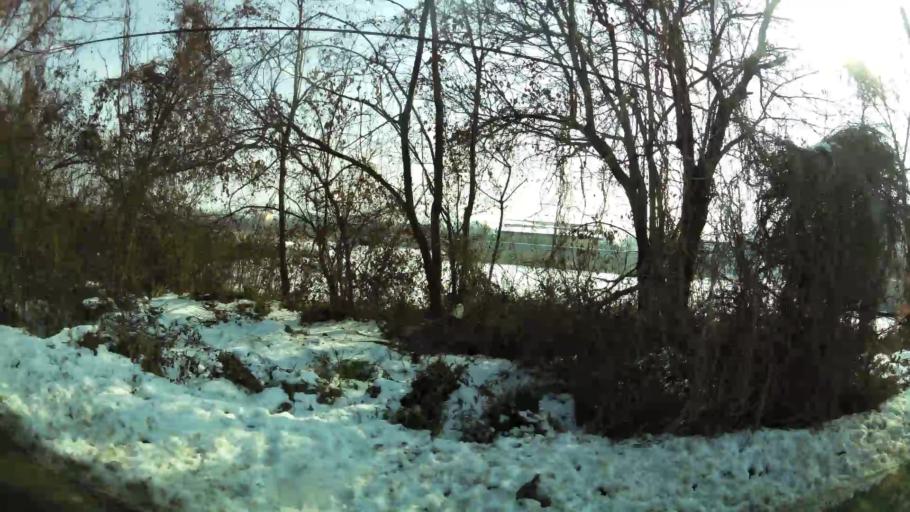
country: MK
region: Suto Orizari
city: Suto Orizare
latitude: 42.0281
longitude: 21.3828
